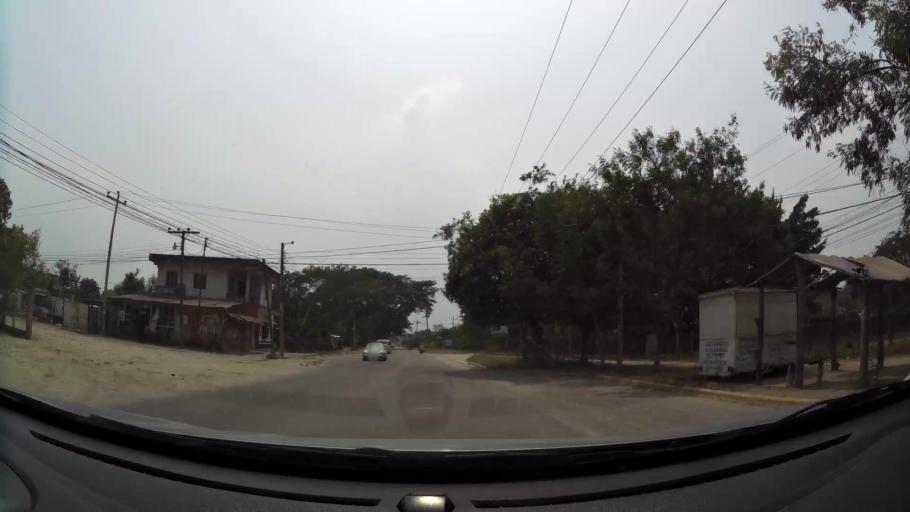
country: HN
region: Cortes
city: La Lima
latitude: 15.4366
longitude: -87.9156
